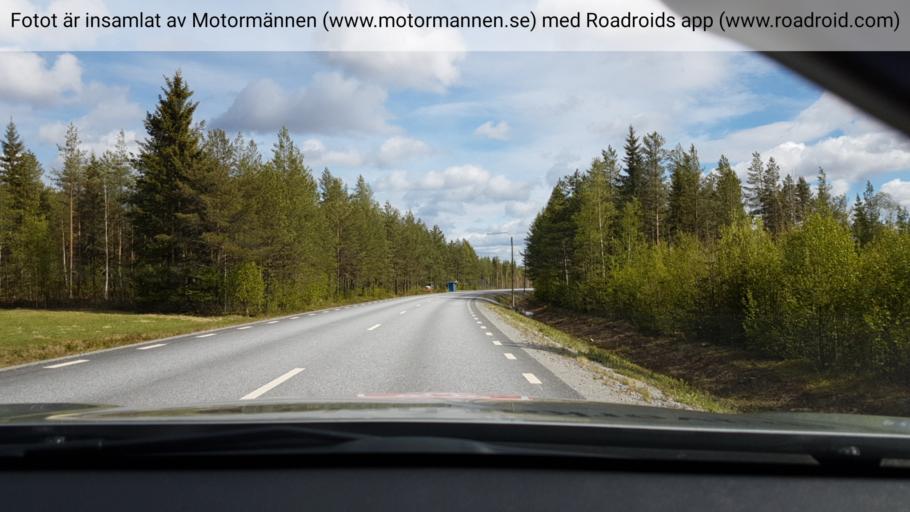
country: SE
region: Vaesterbotten
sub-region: Asele Kommun
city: Insjon
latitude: 64.1402
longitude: 18.0378
